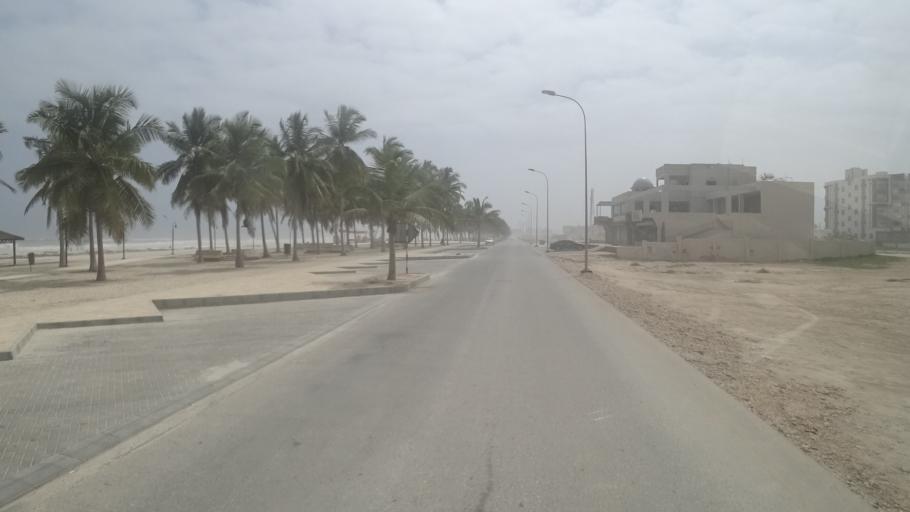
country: OM
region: Zufar
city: Salalah
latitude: 17.0117
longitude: 54.1752
